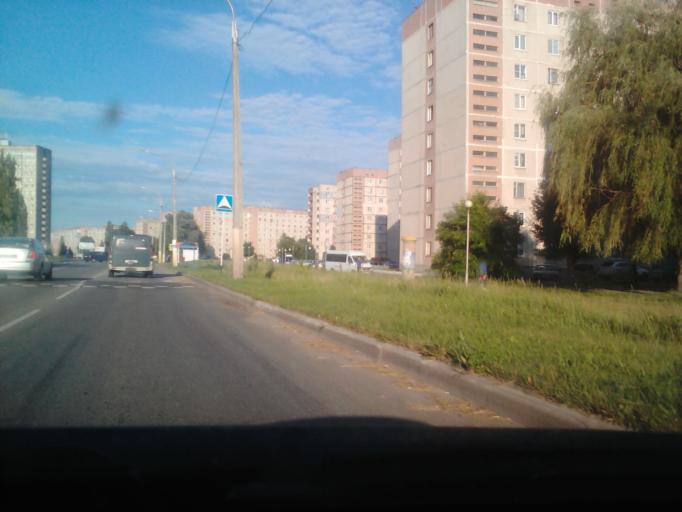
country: RU
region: Kursk
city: Kurchatov
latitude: 51.6531
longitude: 35.6789
